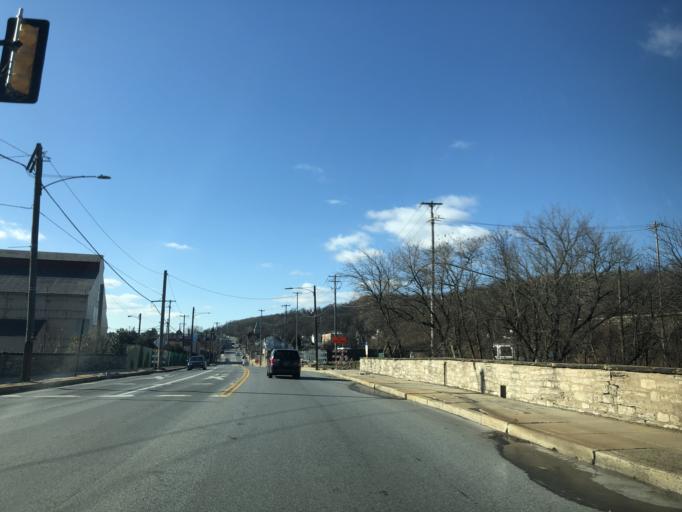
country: US
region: Pennsylvania
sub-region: Chester County
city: Coatesville
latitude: 39.9830
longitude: -75.8243
